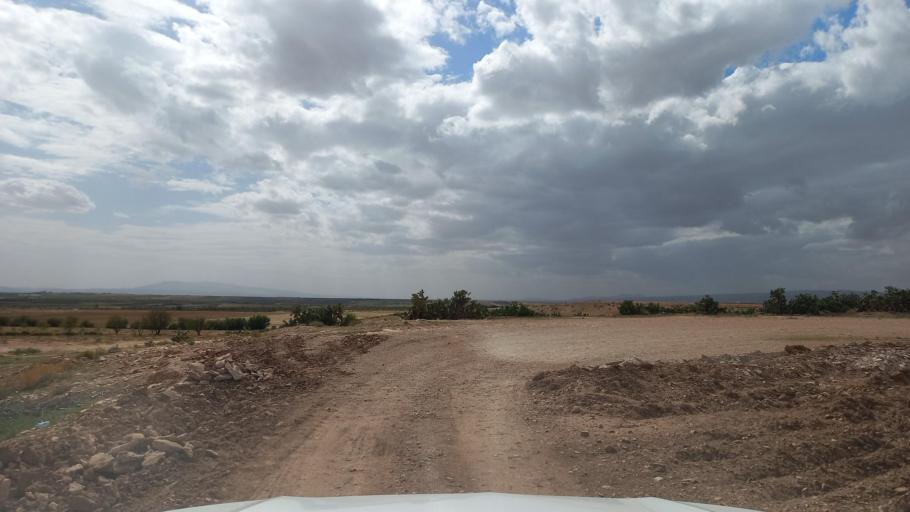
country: TN
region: Al Qasrayn
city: Sbiba
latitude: 35.3812
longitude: 9.0938
